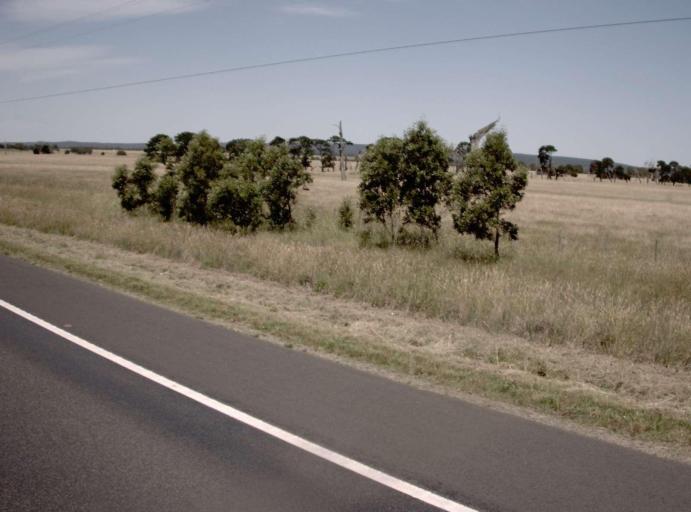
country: AU
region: Victoria
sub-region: Wellington
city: Heyfield
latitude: -38.1589
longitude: 146.7328
